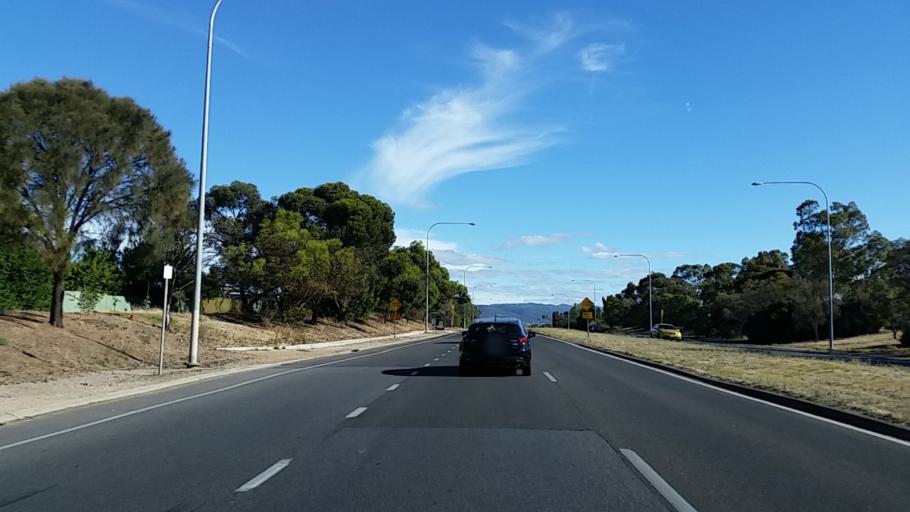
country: AU
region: South Australia
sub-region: Tea Tree Gully
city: Modbury
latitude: -34.8128
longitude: 138.6755
